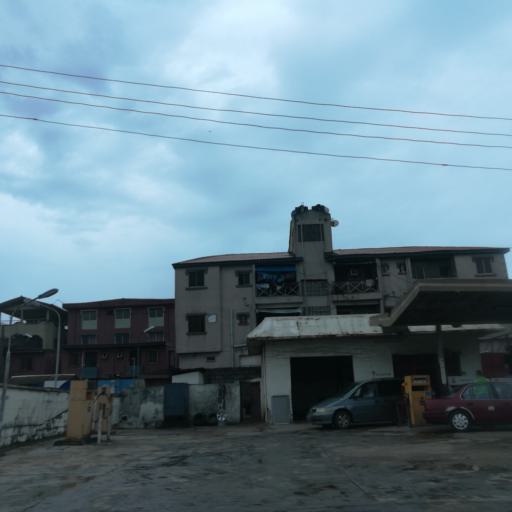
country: NG
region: Lagos
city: Ebute Metta
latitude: 6.4881
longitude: 3.3806
